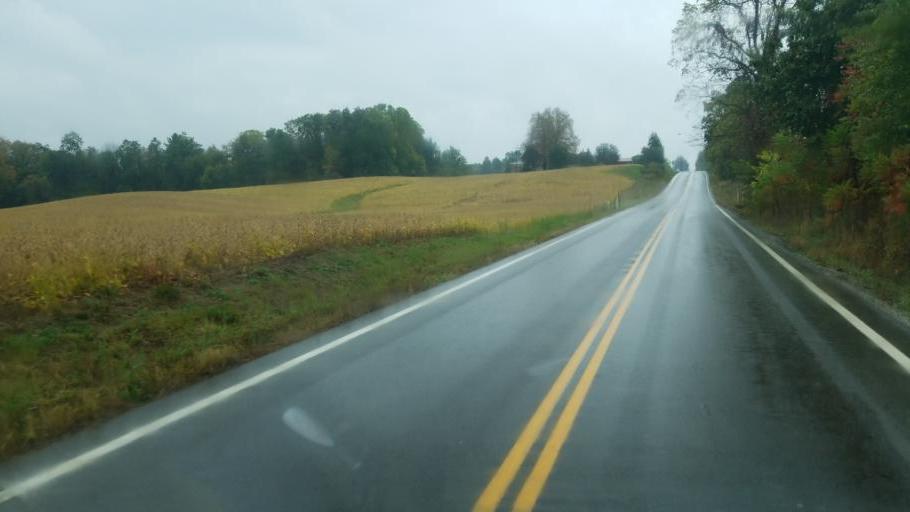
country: US
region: Ohio
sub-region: Richland County
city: Lincoln Heights
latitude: 40.6881
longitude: -82.3783
